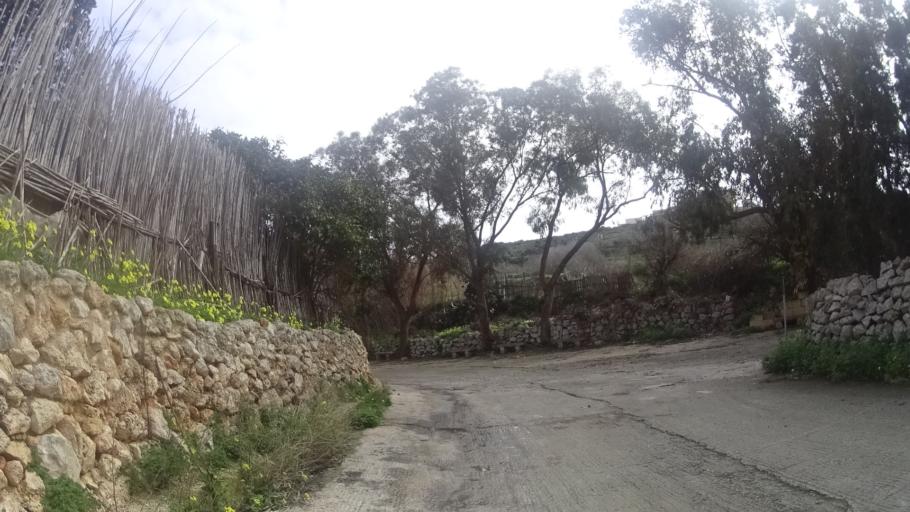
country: MT
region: Il-Qala
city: Qala
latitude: 36.0450
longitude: 14.3068
